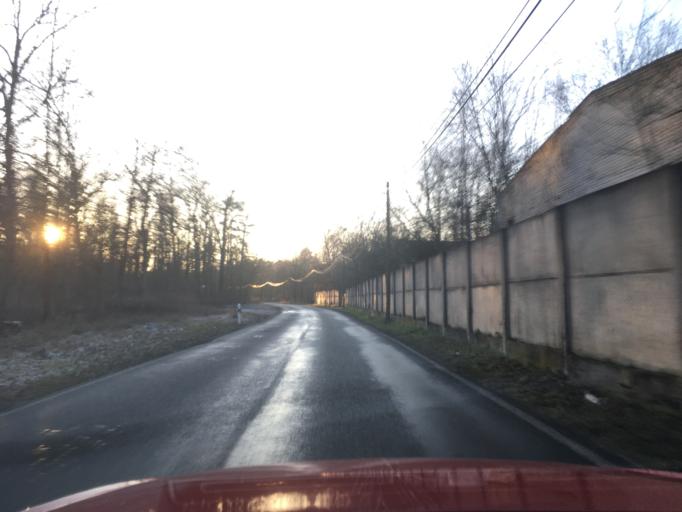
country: DE
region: Saxony-Anhalt
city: Rosslau
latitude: 51.9027
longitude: 12.2793
